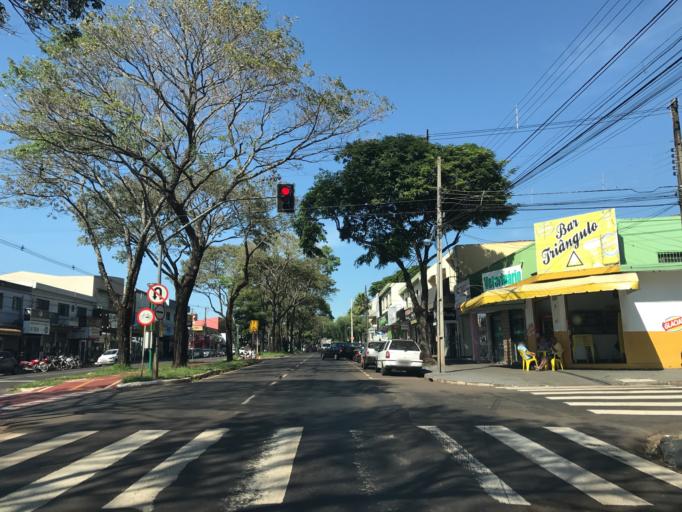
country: BR
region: Parana
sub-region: Maringa
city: Maringa
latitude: -23.4118
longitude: -51.9555
